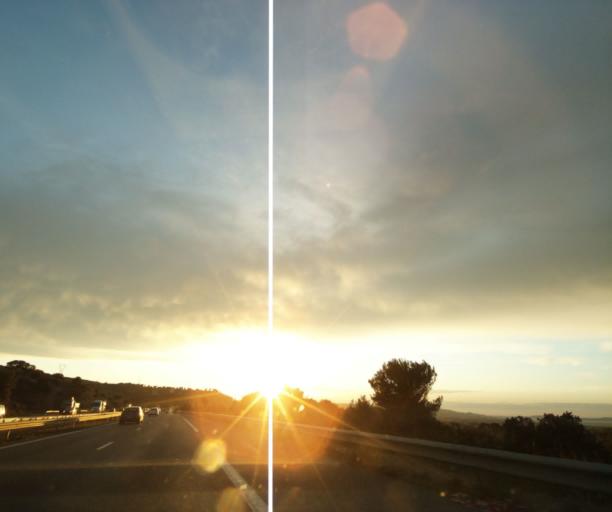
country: FR
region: Provence-Alpes-Cote d'Azur
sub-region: Departement des Bouches-du-Rhone
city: Gignac-la-Nerthe
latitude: 43.3897
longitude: 5.2459
